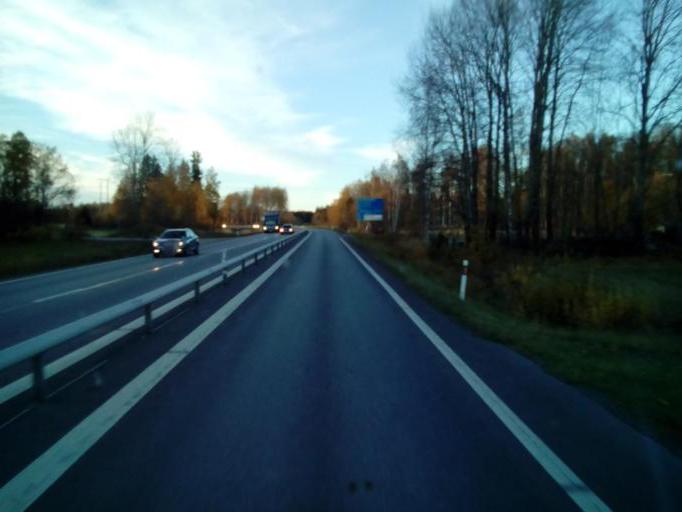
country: SE
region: OErebro
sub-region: Orebro Kommun
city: Orebro
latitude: 59.2024
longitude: 15.2420
